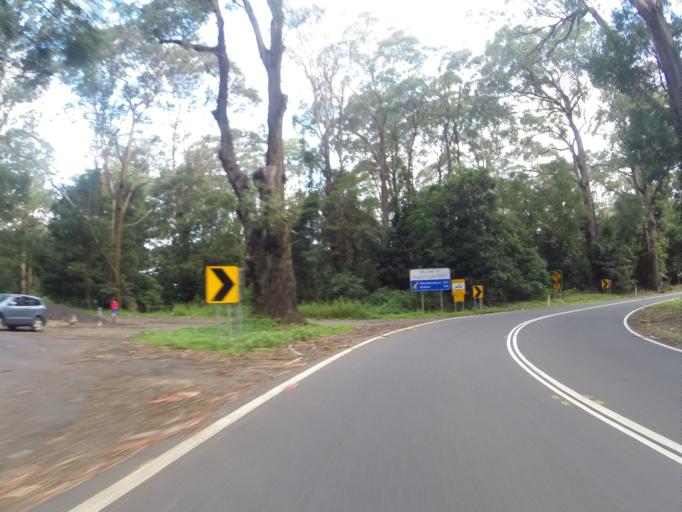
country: AU
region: New South Wales
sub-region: Shellharbour
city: Calderwood
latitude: -34.5572
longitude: 150.6495
